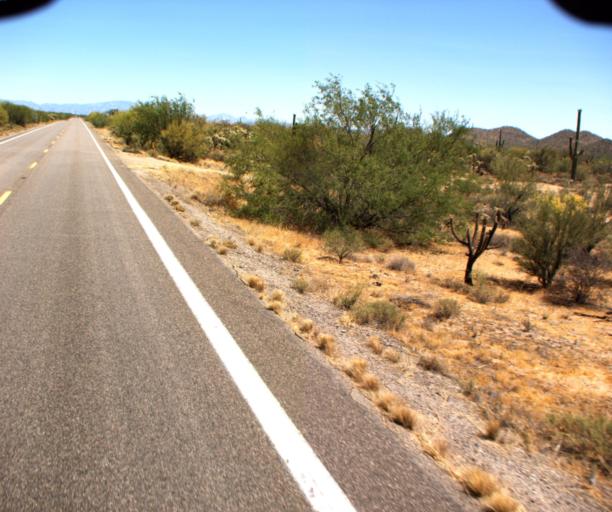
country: US
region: Arizona
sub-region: Pima County
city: Marana
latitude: 32.7578
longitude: -111.1427
